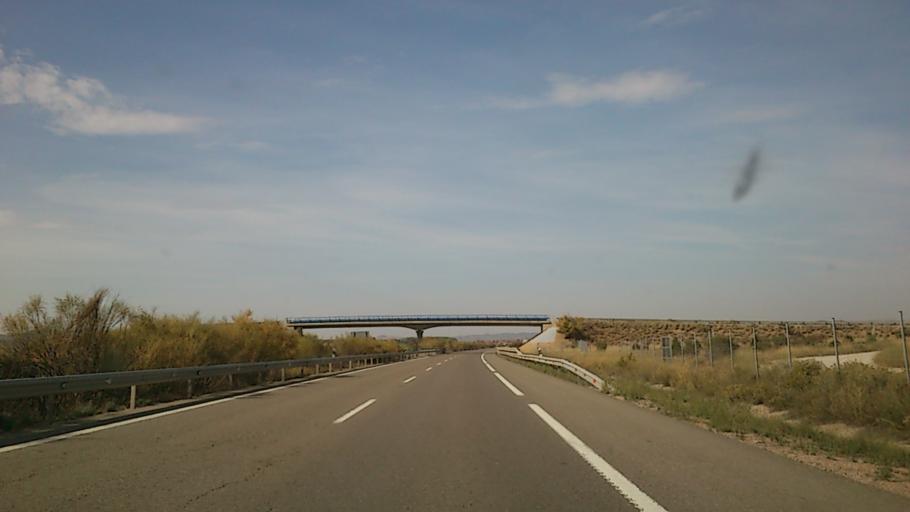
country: ES
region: Aragon
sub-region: Provincia de Teruel
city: Fuentes Claras
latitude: 40.8507
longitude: -1.3096
